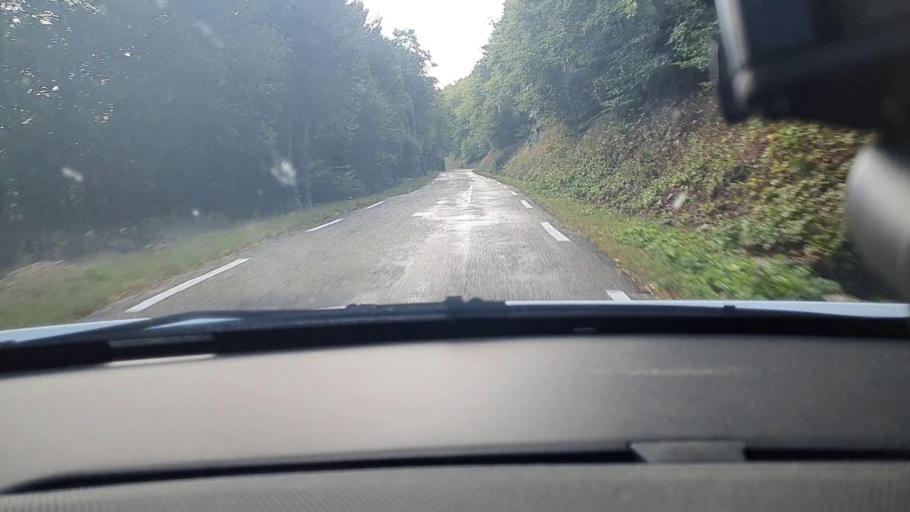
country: FR
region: Languedoc-Roussillon
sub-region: Departement du Gard
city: Branoux-les-Taillades
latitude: 44.3845
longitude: 3.9087
